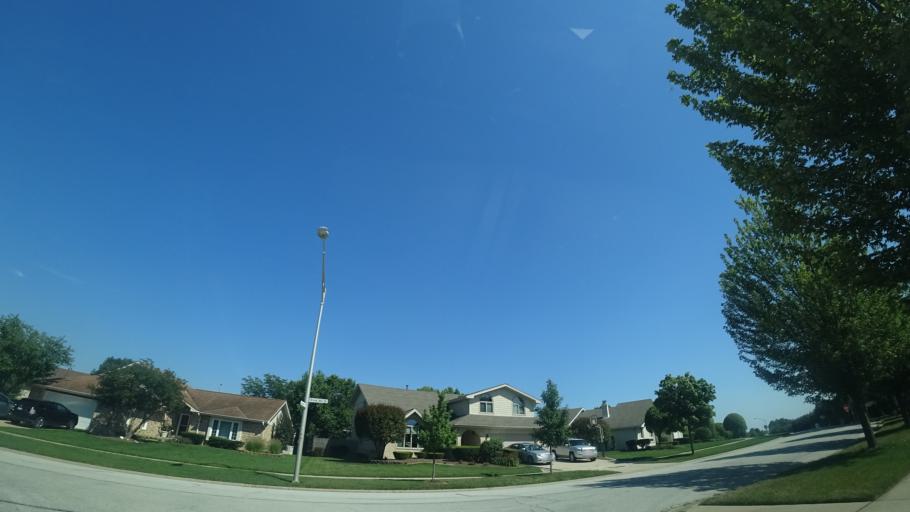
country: US
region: Illinois
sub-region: Will County
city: Homer Glen
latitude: 41.5702
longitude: -87.9050
